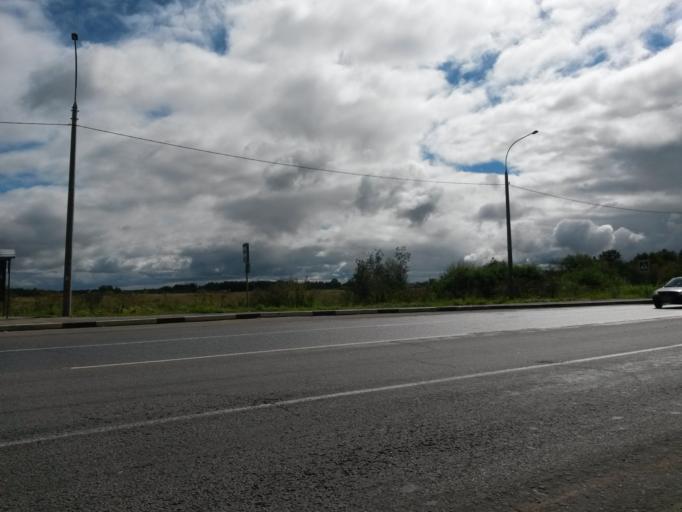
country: RU
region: Jaroslavl
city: Yaroslavl
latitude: 57.6536
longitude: 39.7525
